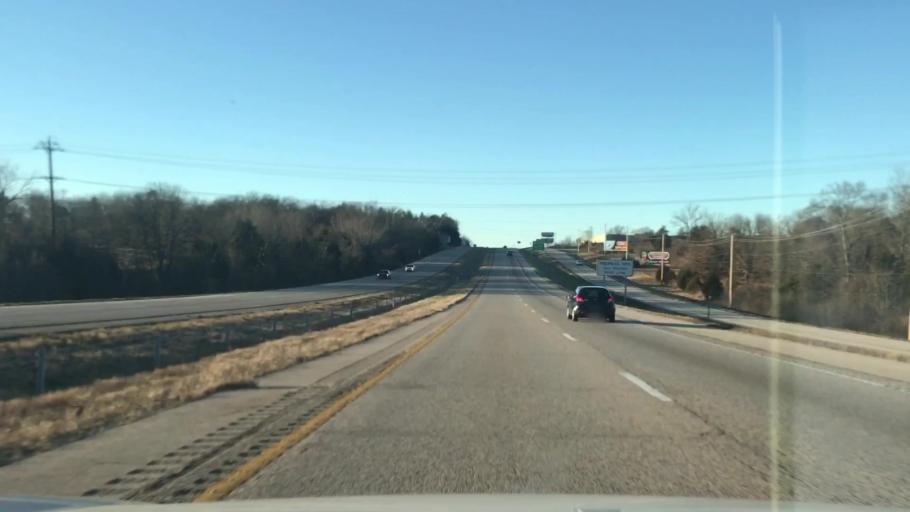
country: US
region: Missouri
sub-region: Franklin County
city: Saint Clair
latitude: 38.3572
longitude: -90.9833
